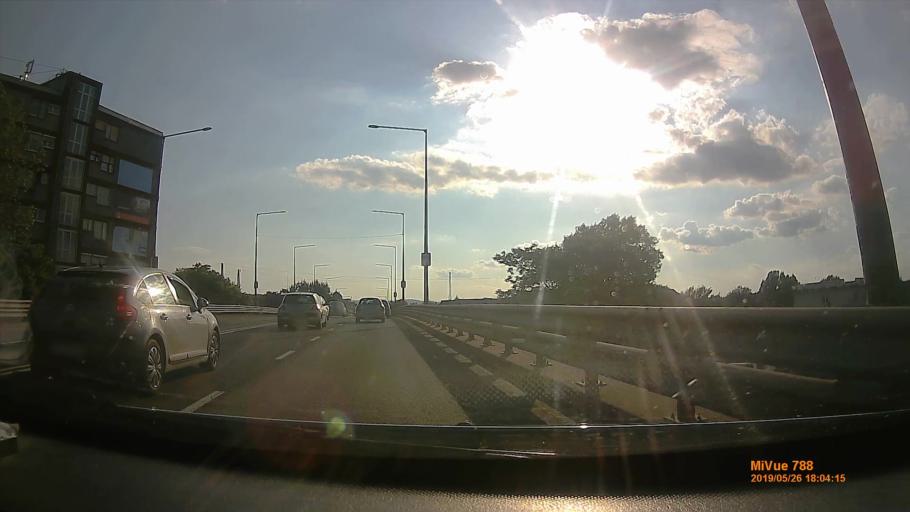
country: HU
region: Borsod-Abauj-Zemplen
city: Miskolc
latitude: 48.1051
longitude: 20.8026
